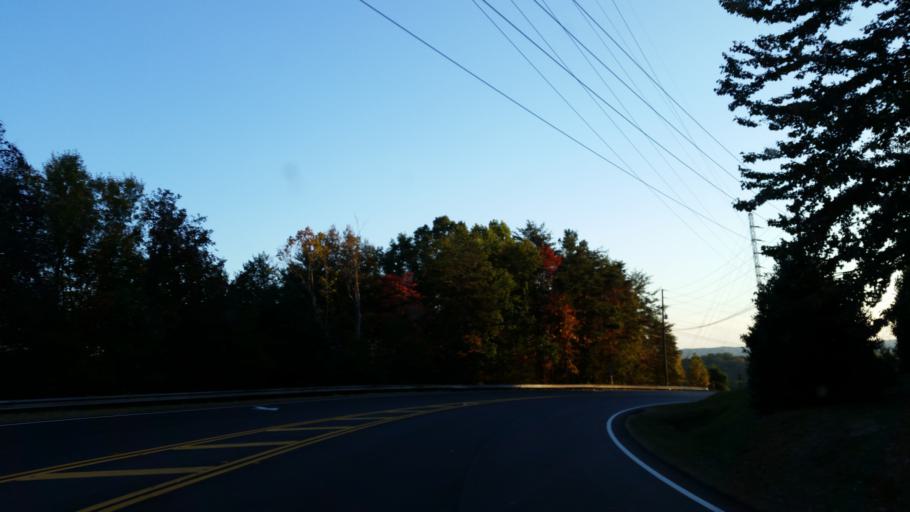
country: US
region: Georgia
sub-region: Lumpkin County
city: Dahlonega
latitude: 34.5232
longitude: -83.9743
